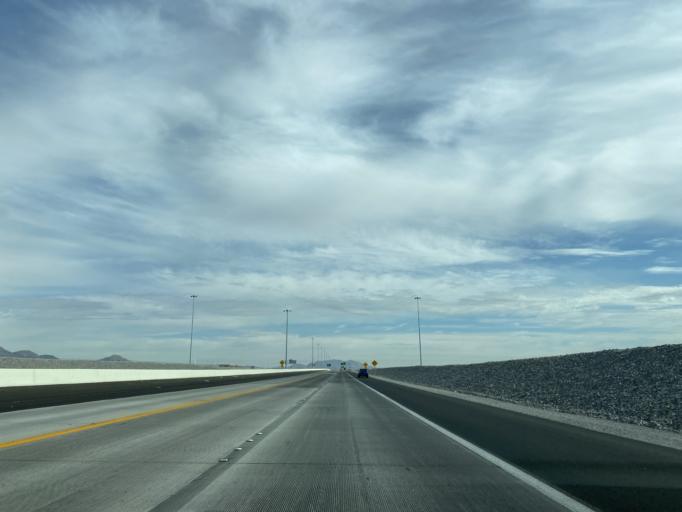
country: US
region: Nevada
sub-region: Clark County
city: Nellis Air Force Base
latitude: 36.2896
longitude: -115.0982
